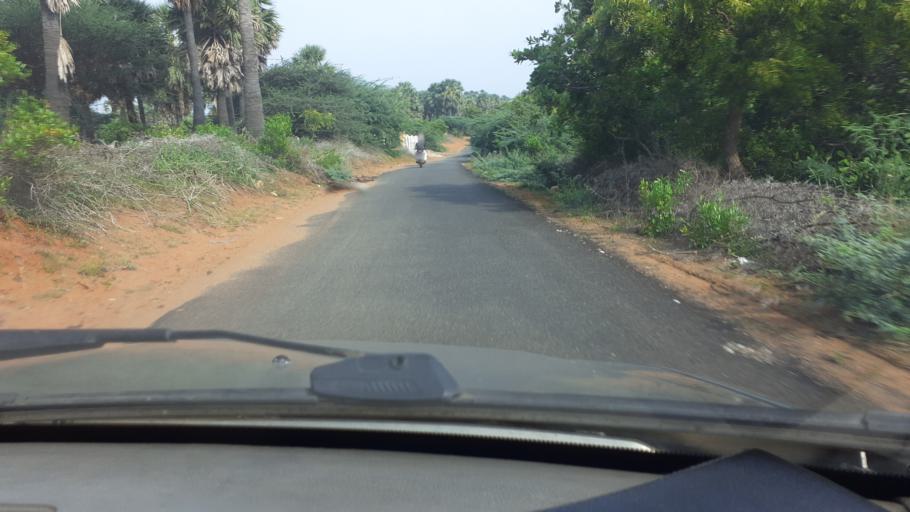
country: IN
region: Tamil Nadu
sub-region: Tirunelveli Kattabo
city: Tisaiyanvilai
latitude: 8.3377
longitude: 77.9444
